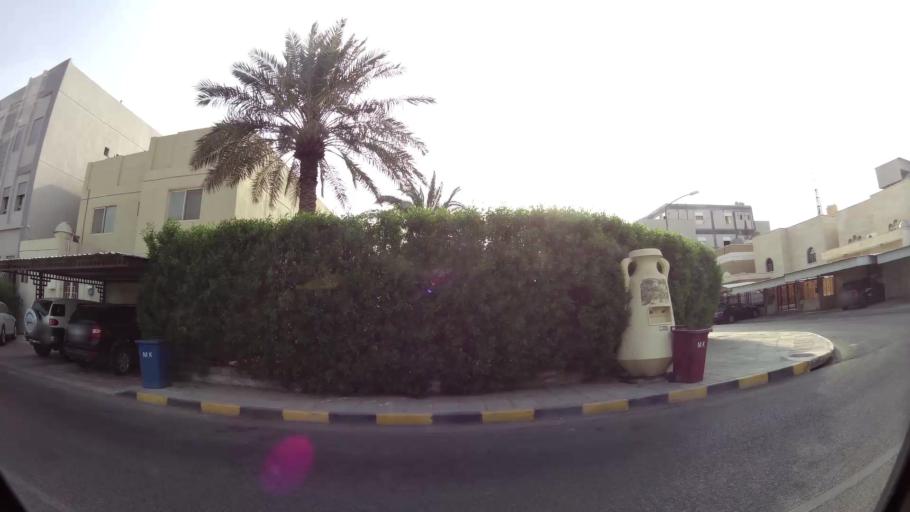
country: KW
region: Mubarak al Kabir
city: Sabah as Salim
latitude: 29.2545
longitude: 48.0524
